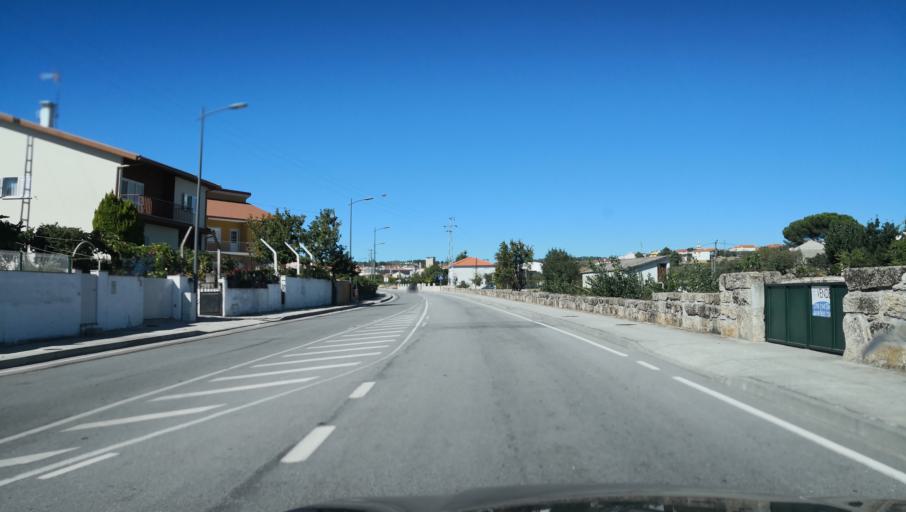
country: PT
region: Vila Real
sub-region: Valpacos
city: Valpacos
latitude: 41.5963
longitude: -7.3059
